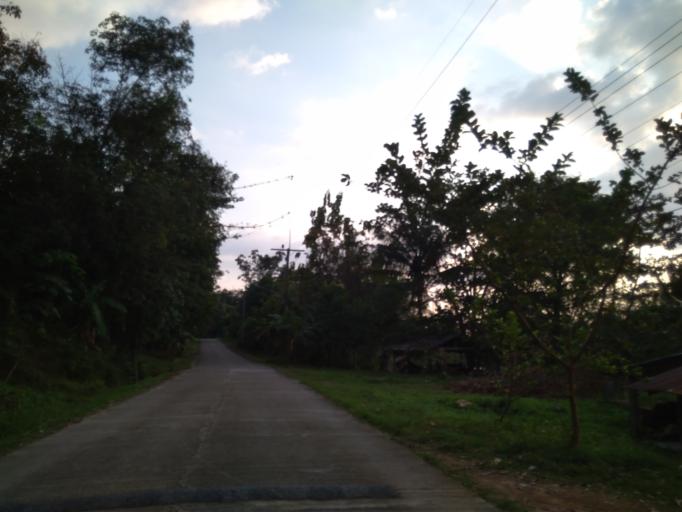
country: TH
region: Phangnga
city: Ko Yao
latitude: 8.1469
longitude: 98.5987
